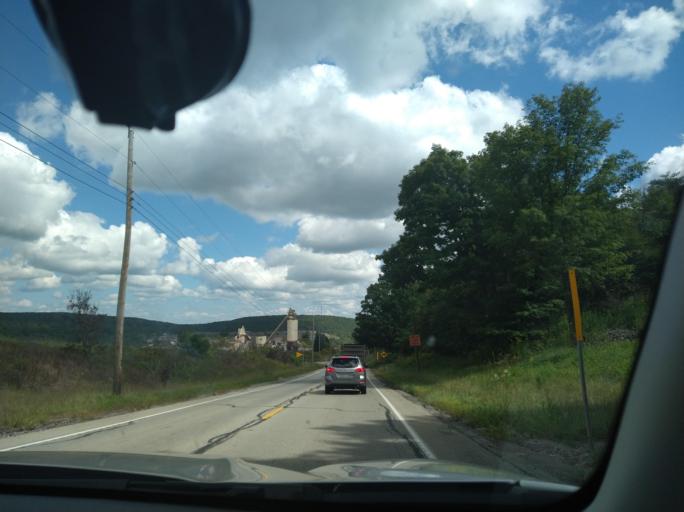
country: US
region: Pennsylvania
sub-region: Westmoreland County
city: Ligonier
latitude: 40.0671
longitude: -79.2617
